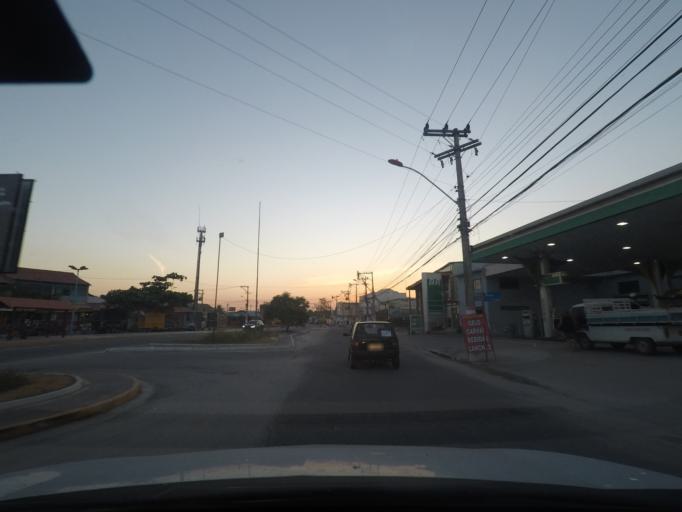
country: BR
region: Rio de Janeiro
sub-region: Niteroi
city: Niteroi
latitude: -22.9587
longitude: -42.9823
